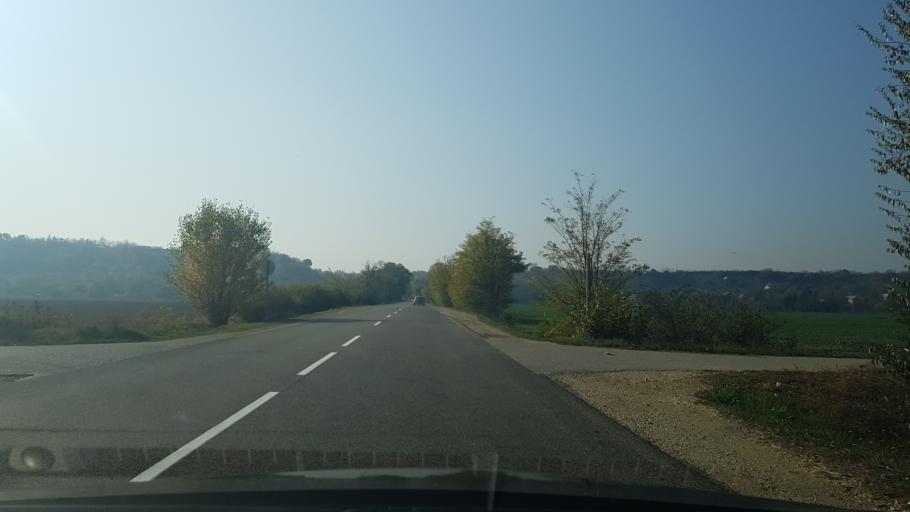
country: HU
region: Fejer
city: Adony
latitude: 47.0872
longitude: 18.8527
